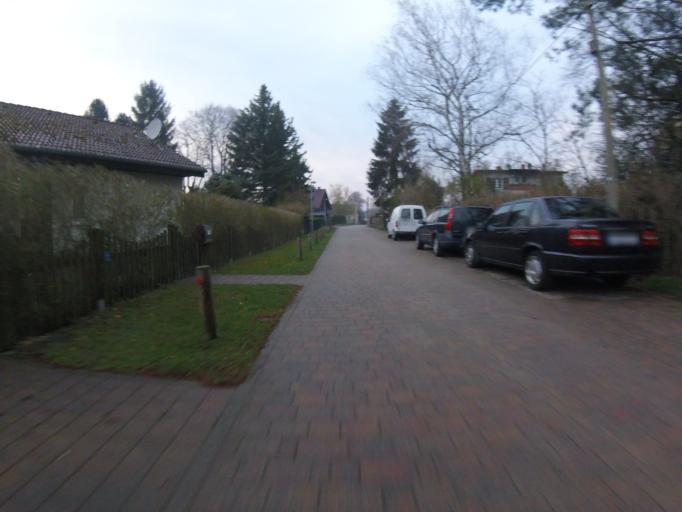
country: DE
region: Brandenburg
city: Konigs Wusterhausen
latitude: 52.2926
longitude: 13.6736
